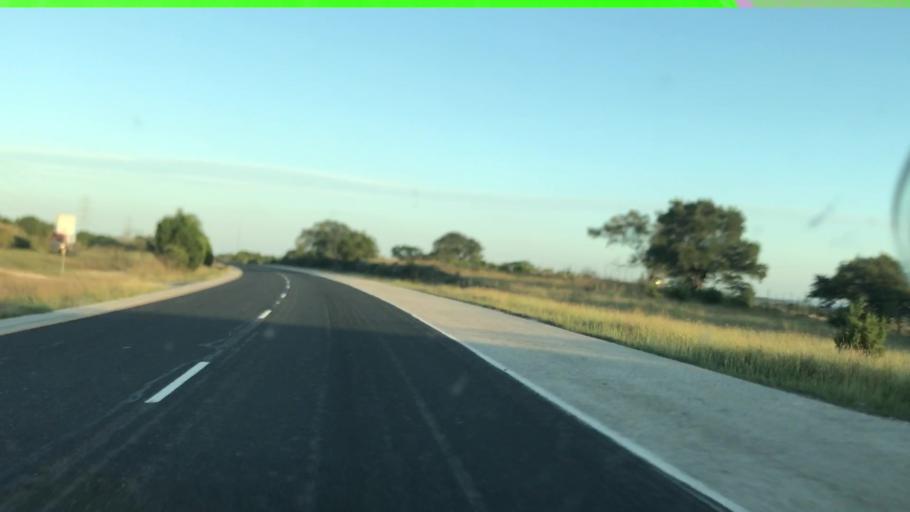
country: US
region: Texas
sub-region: Kerr County
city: Kerrville
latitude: 30.0584
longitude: -99.0460
